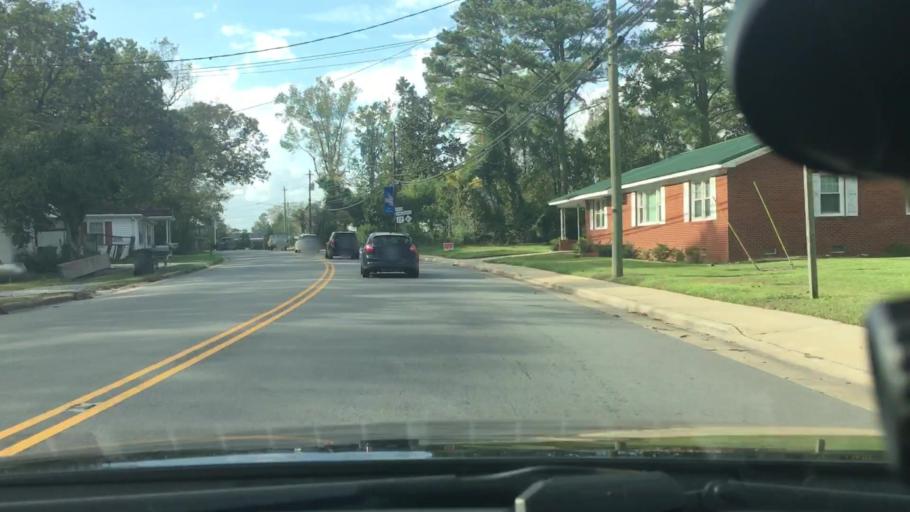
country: US
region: North Carolina
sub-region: Craven County
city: Vanceboro
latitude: 35.2975
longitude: -77.1493
